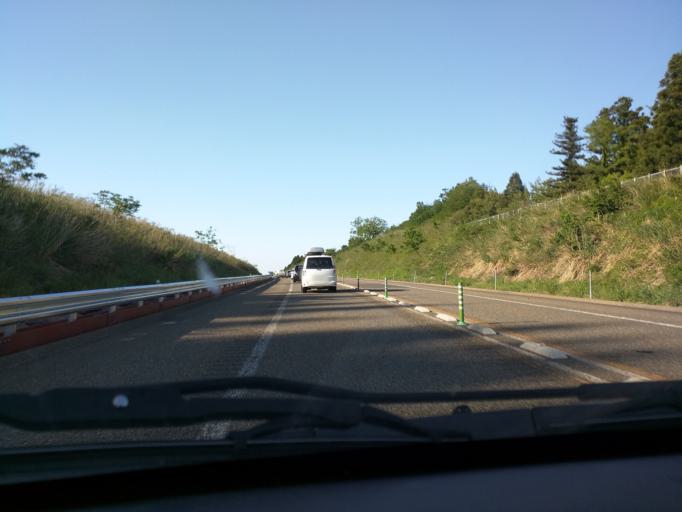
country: JP
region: Niigata
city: Arai
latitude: 37.0340
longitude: 138.2305
